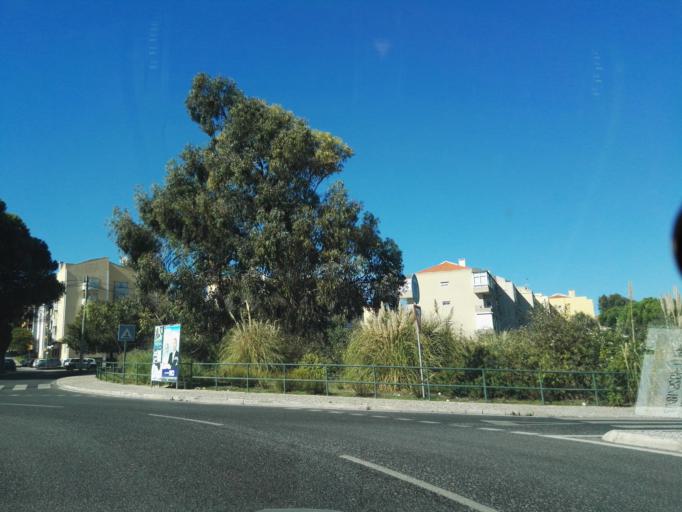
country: PT
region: Lisbon
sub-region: Sintra
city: Rio de Mouro
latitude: 38.7878
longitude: -9.3288
